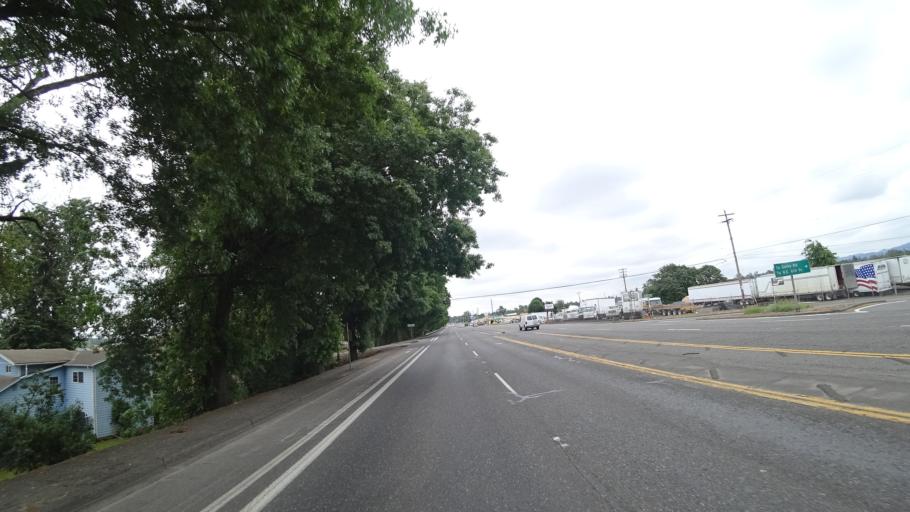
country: US
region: Washington
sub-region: Clark County
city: Vancouver
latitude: 45.5913
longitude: -122.6668
